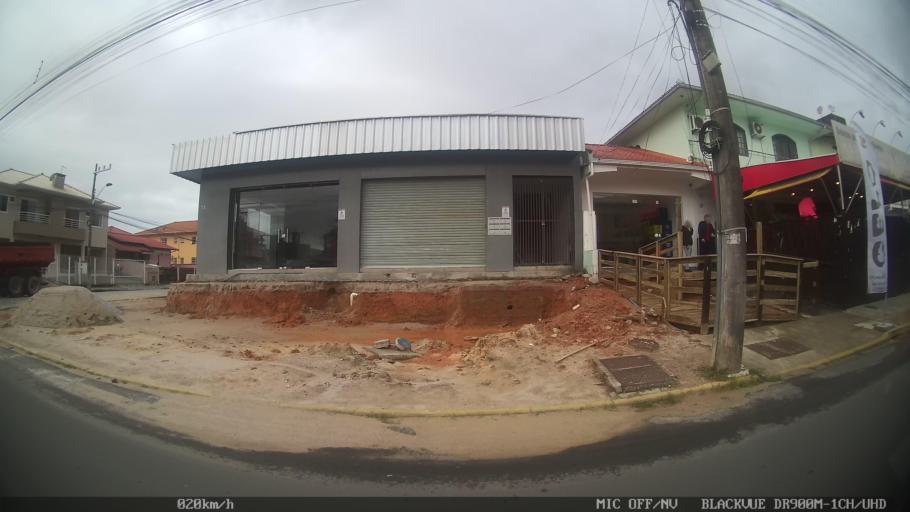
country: BR
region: Santa Catarina
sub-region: Biguacu
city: Biguacu
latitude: -27.5083
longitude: -48.6518
